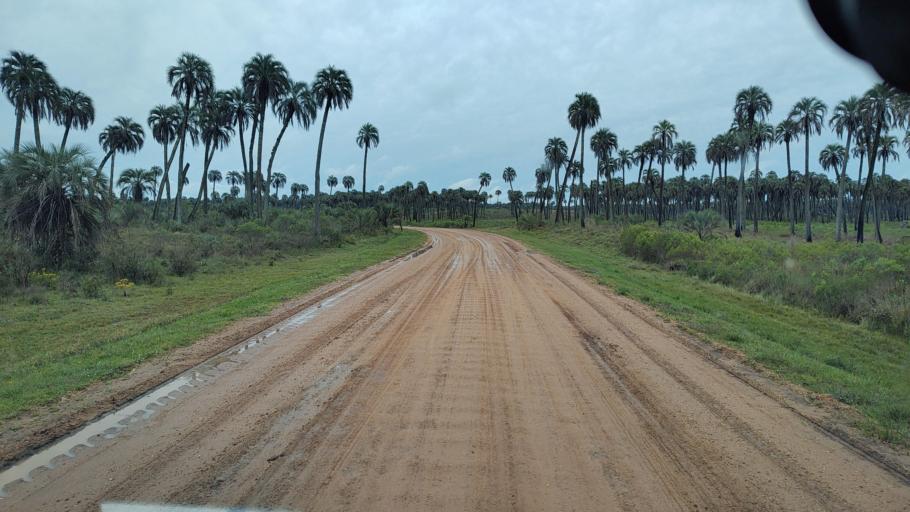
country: AR
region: Entre Rios
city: Ubajay
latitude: -31.8533
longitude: -58.3166
